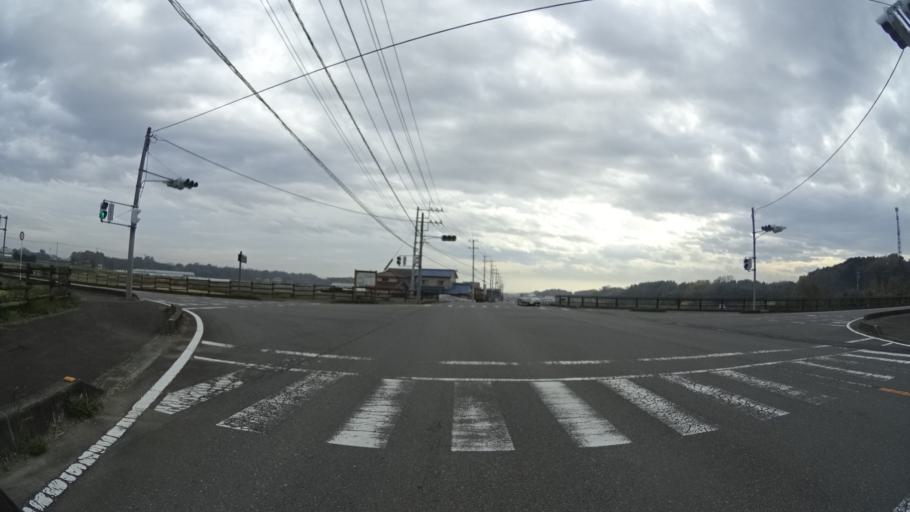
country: JP
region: Gunma
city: Maebashi-shi
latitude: 36.4334
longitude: 139.1620
